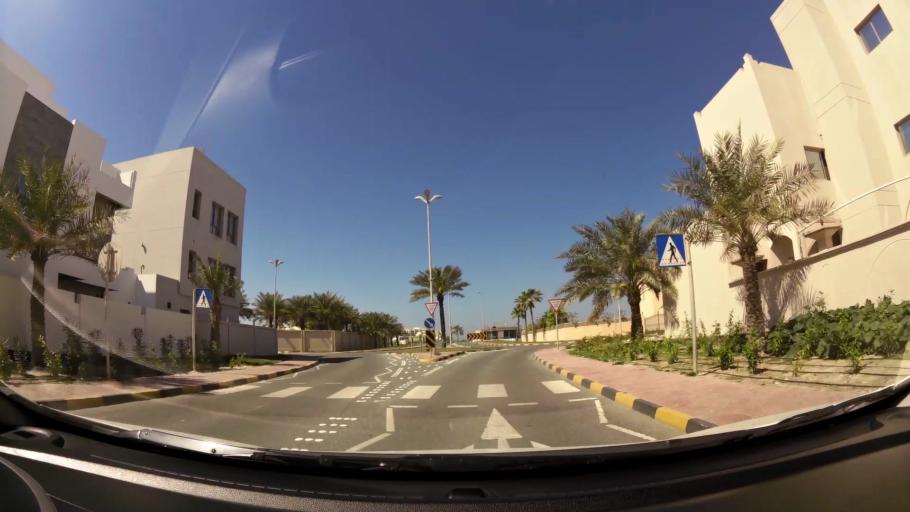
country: BH
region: Muharraq
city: Al Hadd
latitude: 26.2919
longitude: 50.6741
